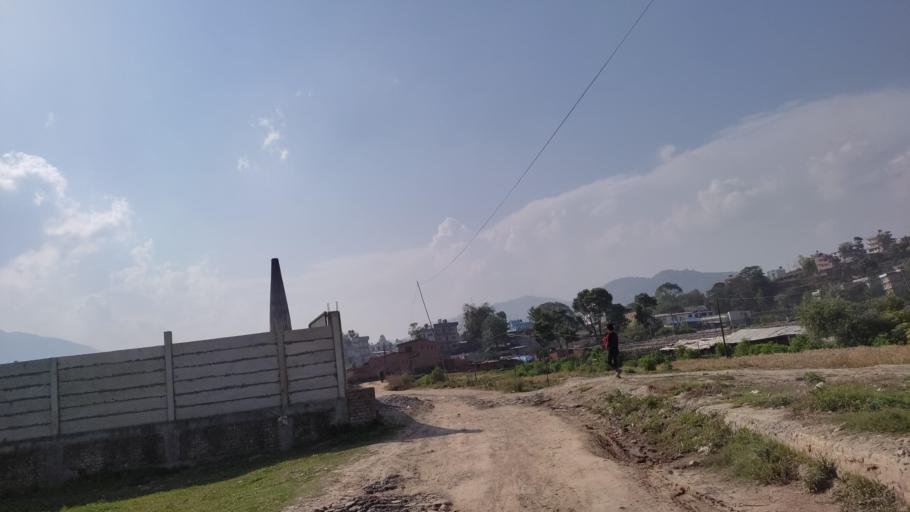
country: NP
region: Central Region
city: Kirtipur
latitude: 27.6791
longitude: 85.2637
